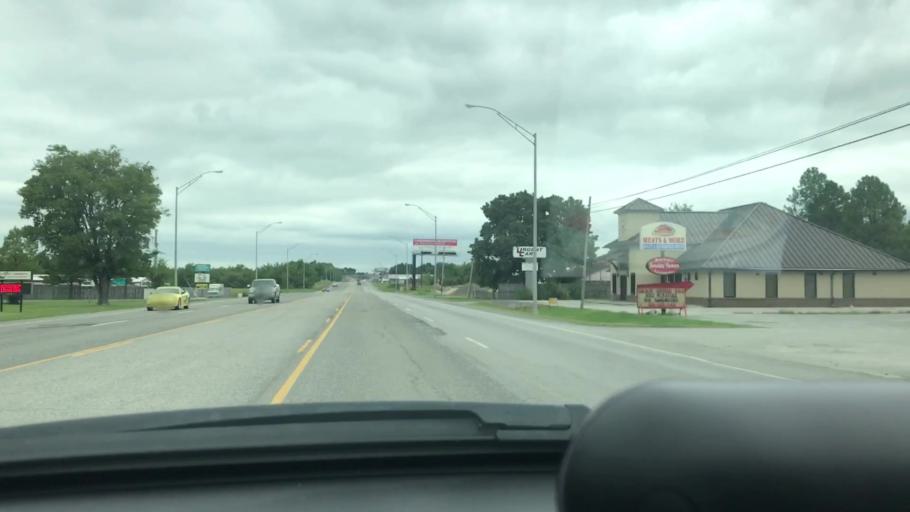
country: US
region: Oklahoma
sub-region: Wagoner County
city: Wagoner
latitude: 35.9471
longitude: -95.3952
